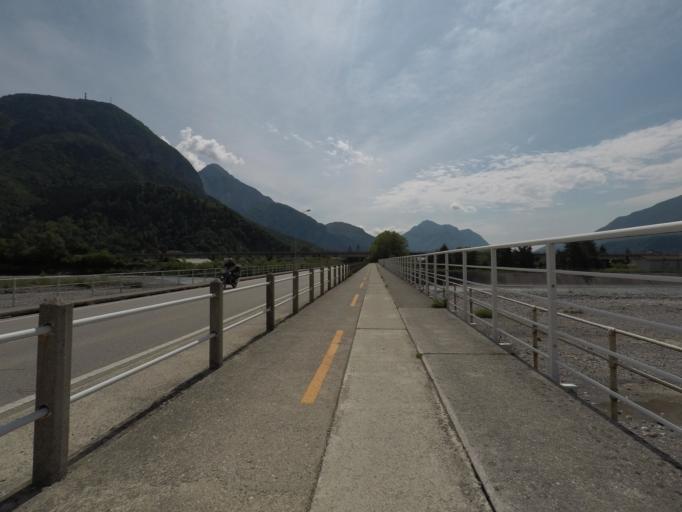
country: IT
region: Friuli Venezia Giulia
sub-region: Provincia di Udine
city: Tolmezzo
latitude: 46.4095
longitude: 13.0058
